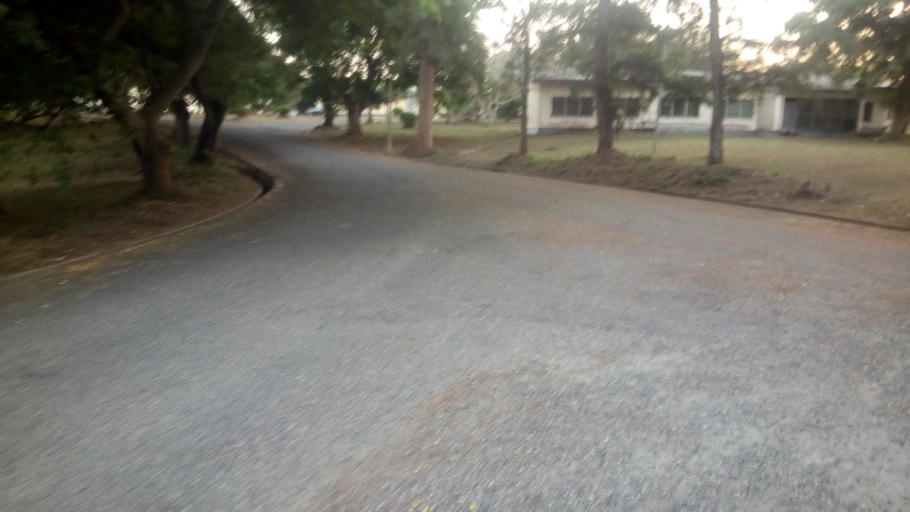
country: GH
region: Central
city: Cape Coast
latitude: 5.1105
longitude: -1.2830
